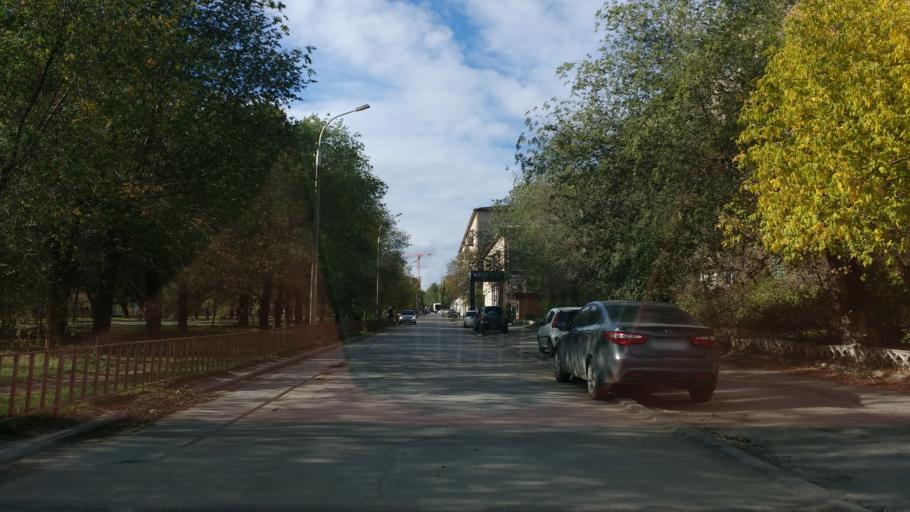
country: RU
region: Volgograd
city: Krasnoslobodsk
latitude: 48.7686
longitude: 44.5534
